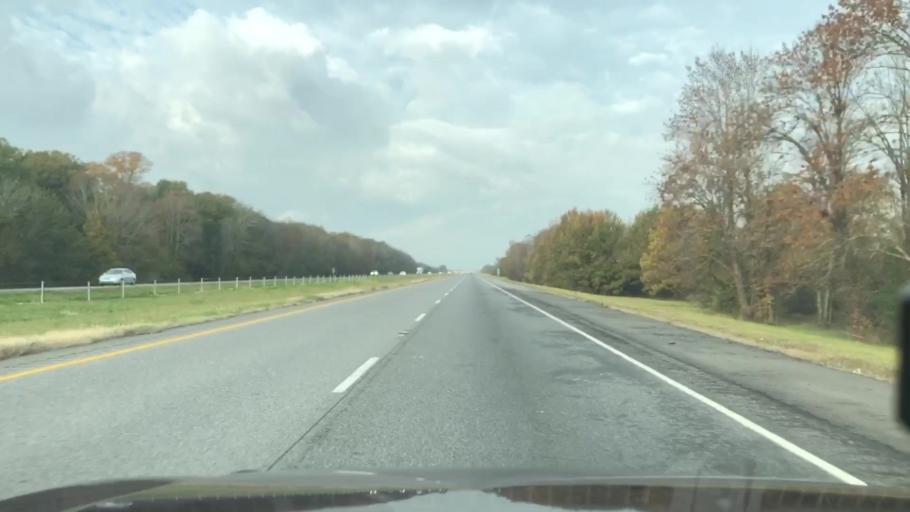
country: US
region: Louisiana
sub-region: Richland Parish
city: Delhi
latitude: 32.4261
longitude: -91.3830
